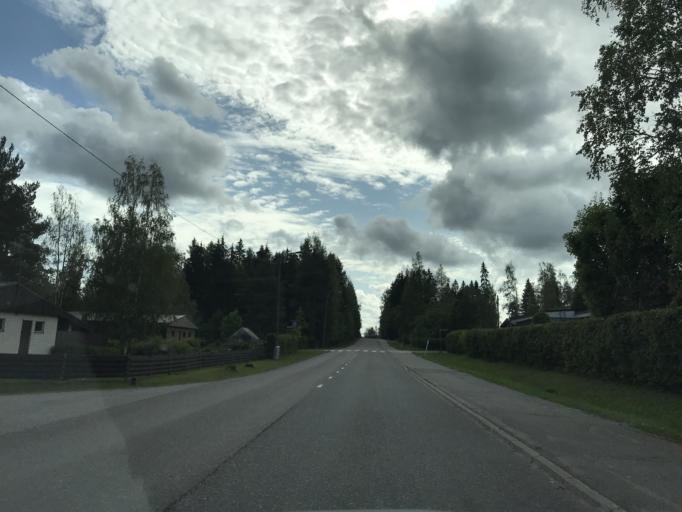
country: FI
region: Paijanne Tavastia
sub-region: Lahti
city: Orimattila
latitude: 60.8151
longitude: 25.7243
